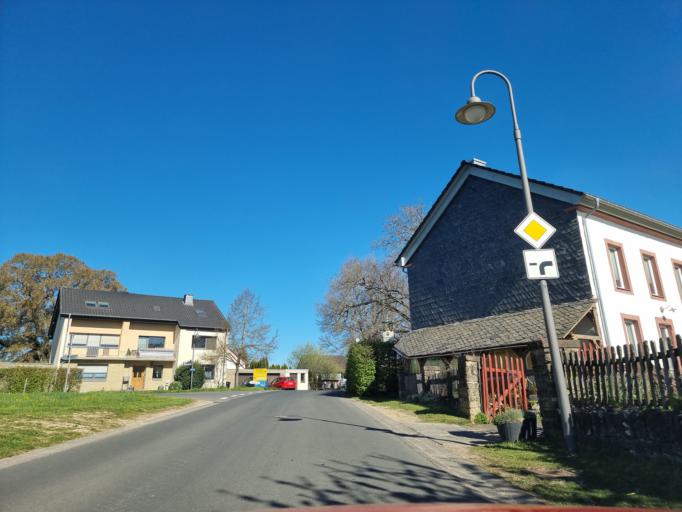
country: DE
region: Rheinland-Pfalz
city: Idenheim
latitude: 49.8975
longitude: 6.5702
